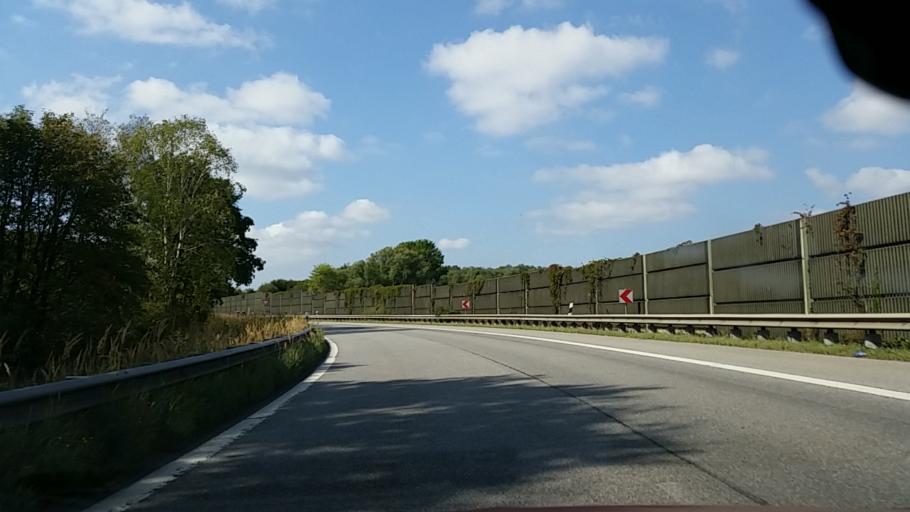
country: DE
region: Hamburg
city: Rothenburgsort
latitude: 53.5086
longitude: 10.0788
